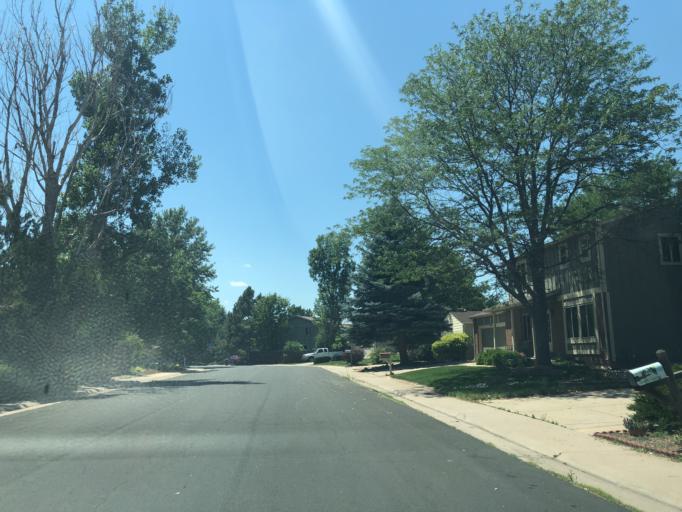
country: US
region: Colorado
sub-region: Arapahoe County
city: Dove Valley
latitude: 39.6237
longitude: -104.7770
